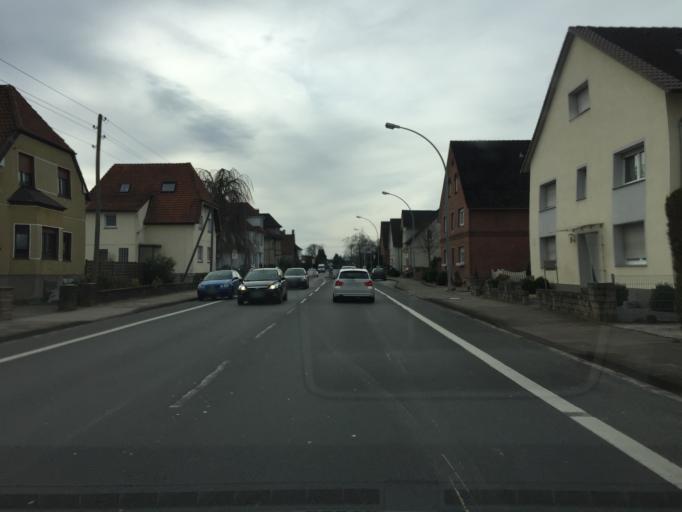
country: DE
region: North Rhine-Westphalia
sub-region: Regierungsbezirk Detmold
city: Bad Salzuflen
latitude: 52.0346
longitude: 8.7572
